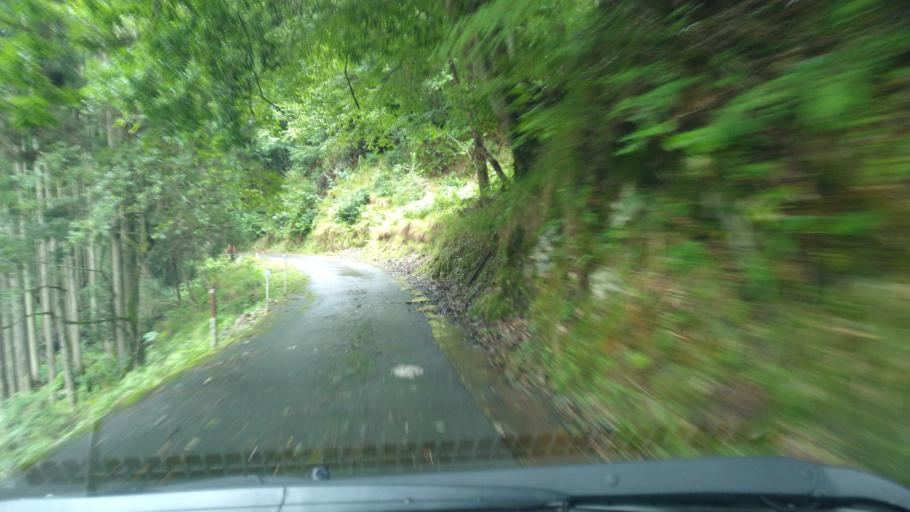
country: JP
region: Kyoto
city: Ayabe
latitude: 35.2333
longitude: 135.2675
